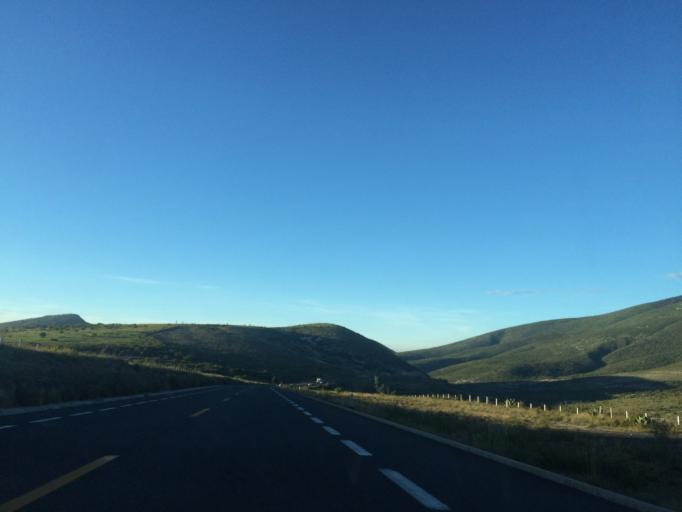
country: MX
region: Puebla
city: Morelos Canada
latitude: 18.6889
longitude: -97.4613
